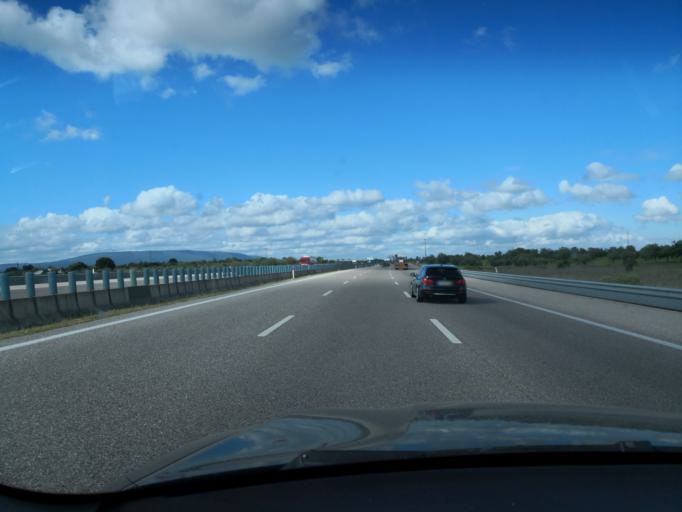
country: PT
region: Santarem
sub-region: Alcanena
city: Alcanena
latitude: 39.4127
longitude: -8.6366
